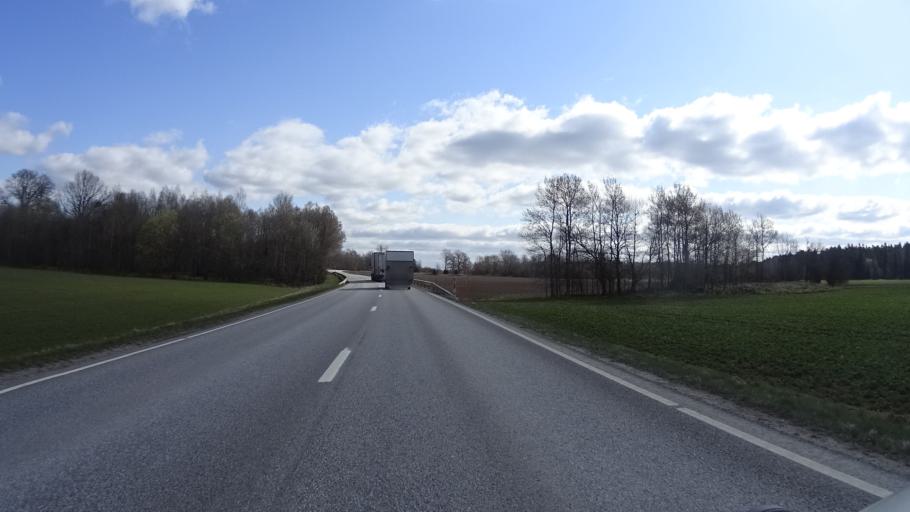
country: SE
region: OEstergoetland
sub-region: Mjolby Kommun
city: Mantorp
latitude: 58.3766
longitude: 15.2676
